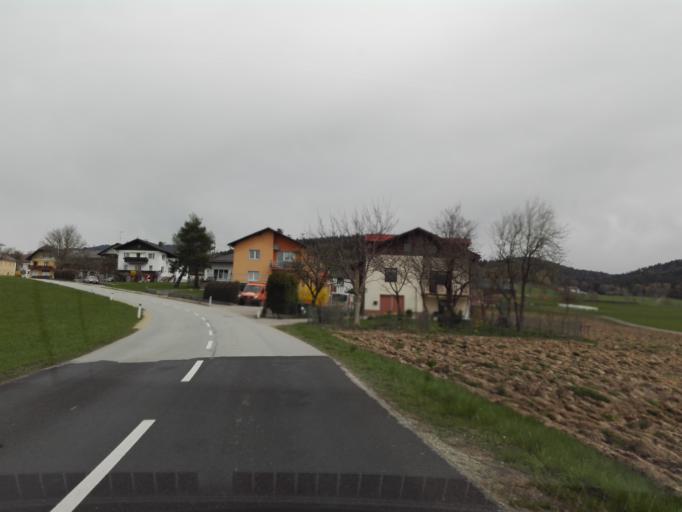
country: AT
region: Upper Austria
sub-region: Politischer Bezirk Rohrbach
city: Ulrichsberg
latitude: 48.6857
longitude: 13.9106
